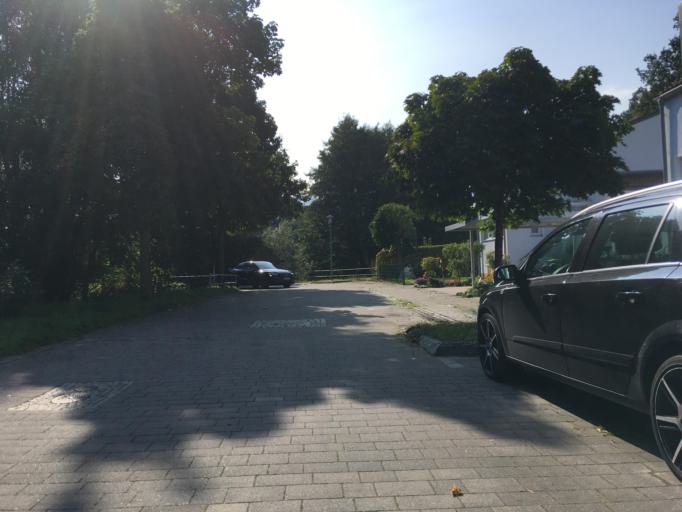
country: DE
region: Brandenburg
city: Wandlitz
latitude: 52.6781
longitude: 13.4337
